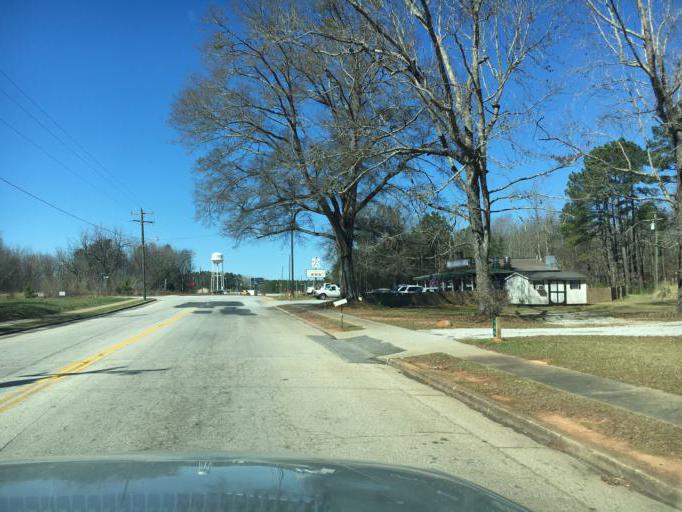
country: US
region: South Carolina
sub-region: Greenwood County
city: Ninety Six
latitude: 34.3138
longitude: -81.9898
